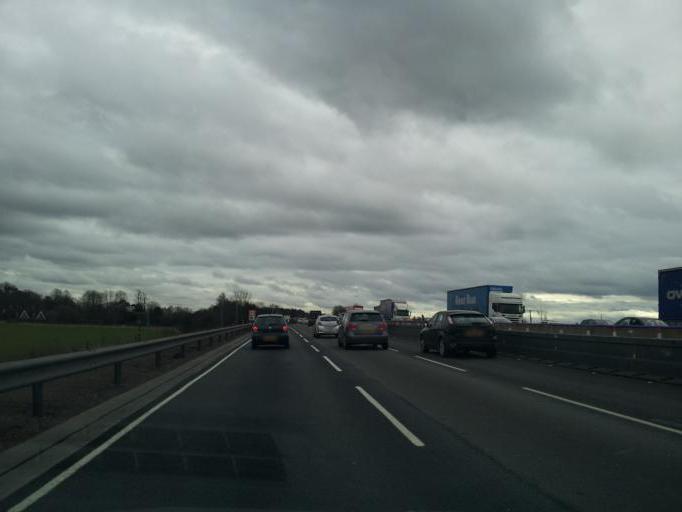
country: GB
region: England
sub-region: Staffordshire
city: Penkridge
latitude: 52.7394
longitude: -2.0985
